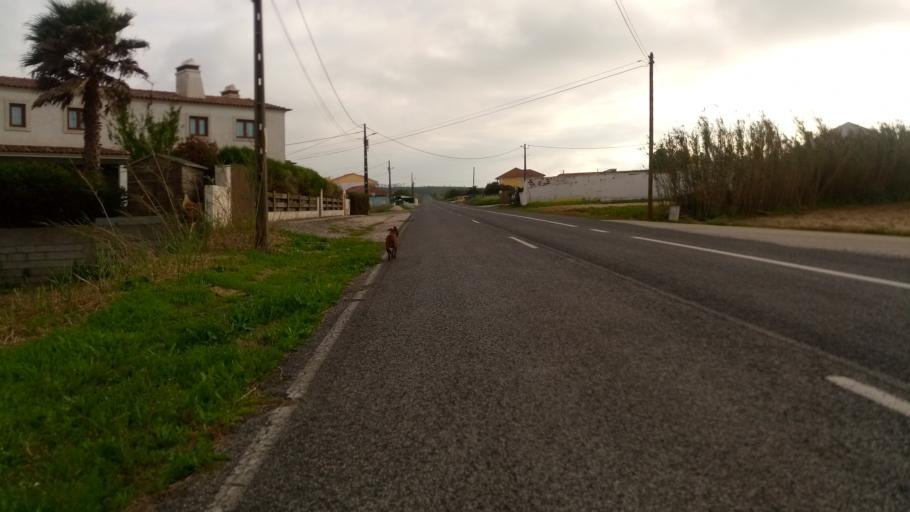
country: PT
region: Leiria
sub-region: Caldas da Rainha
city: Caldas da Rainha
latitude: 39.4817
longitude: -9.1837
